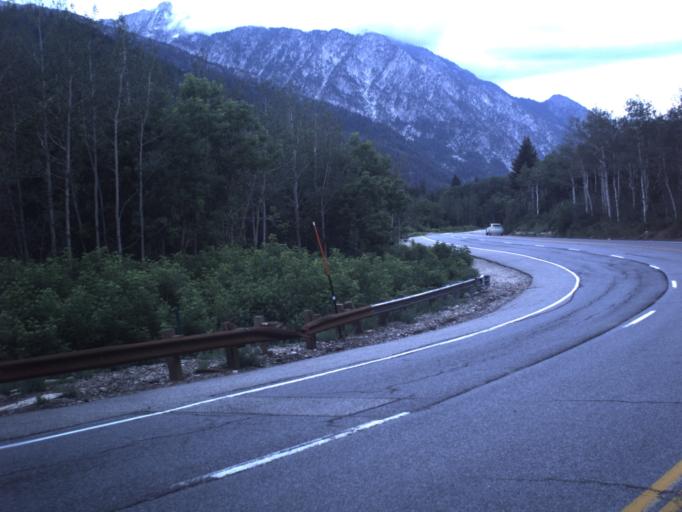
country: US
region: Utah
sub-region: Salt Lake County
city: Granite
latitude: 40.5762
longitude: -111.6819
